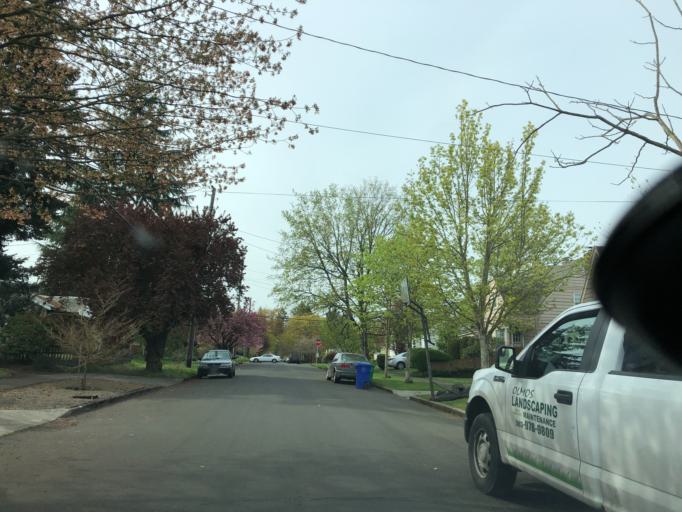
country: US
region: Oregon
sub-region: Multnomah County
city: Portland
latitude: 45.5575
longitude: -122.6276
